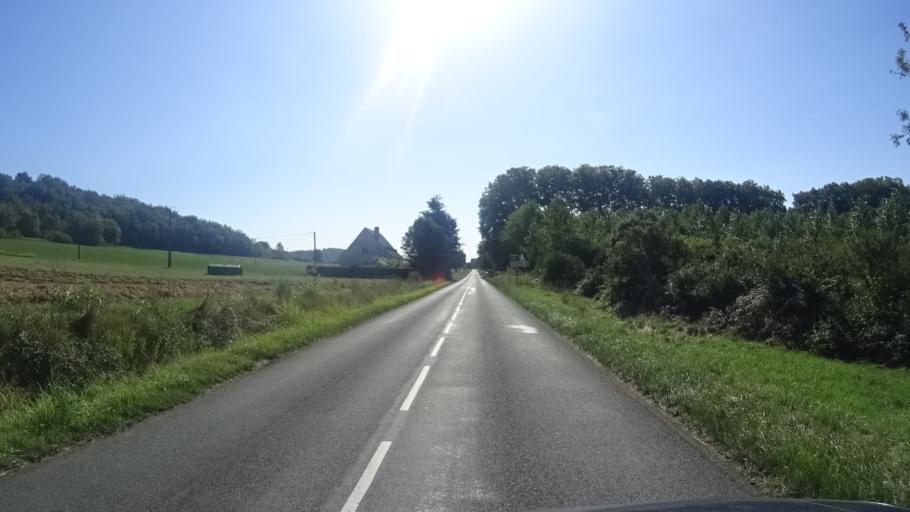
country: FR
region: Aquitaine
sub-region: Departement de la Dordogne
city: Sourzac
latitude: 45.0168
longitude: 0.4361
